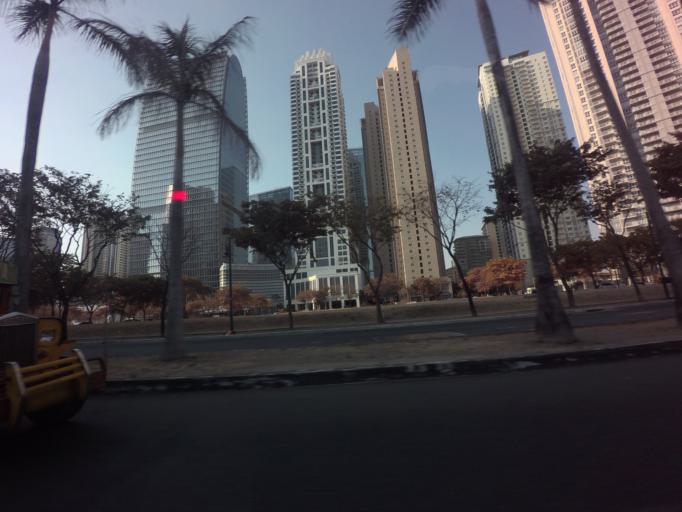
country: PH
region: Metro Manila
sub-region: Makati City
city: Makati City
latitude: 14.5456
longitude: 121.0512
